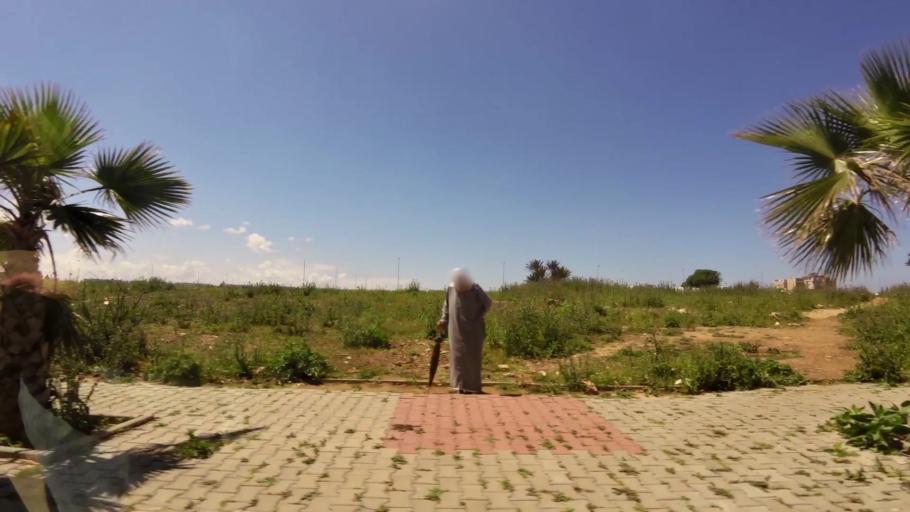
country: MA
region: Grand Casablanca
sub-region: Nouaceur
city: Dar Bouazza
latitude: 33.5241
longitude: -7.8189
